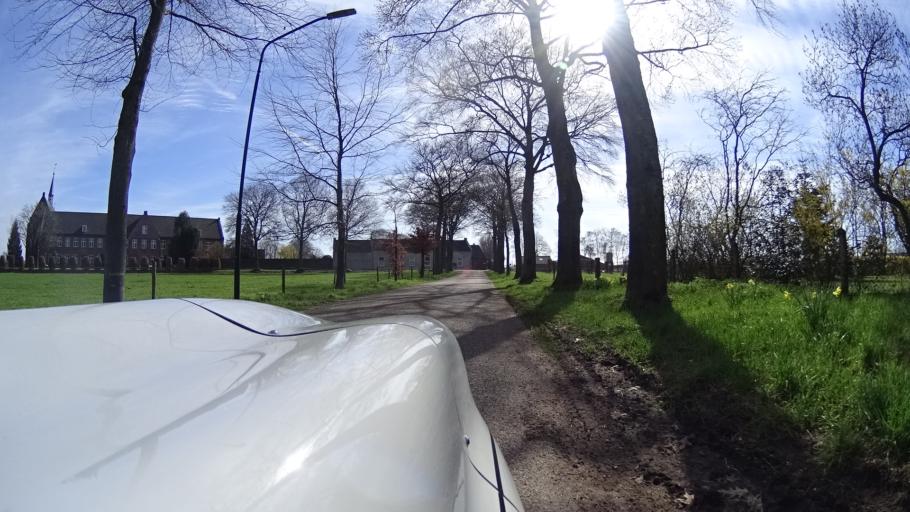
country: NL
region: North Brabant
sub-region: Gemeente Cuijk
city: Cuijk
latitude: 51.7132
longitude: 5.9149
